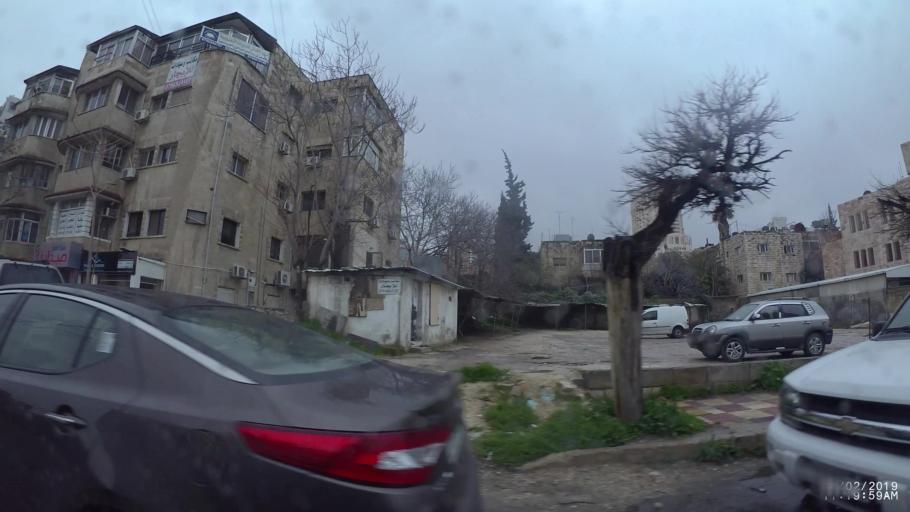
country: JO
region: Amman
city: Amman
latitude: 31.9558
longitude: 35.9119
